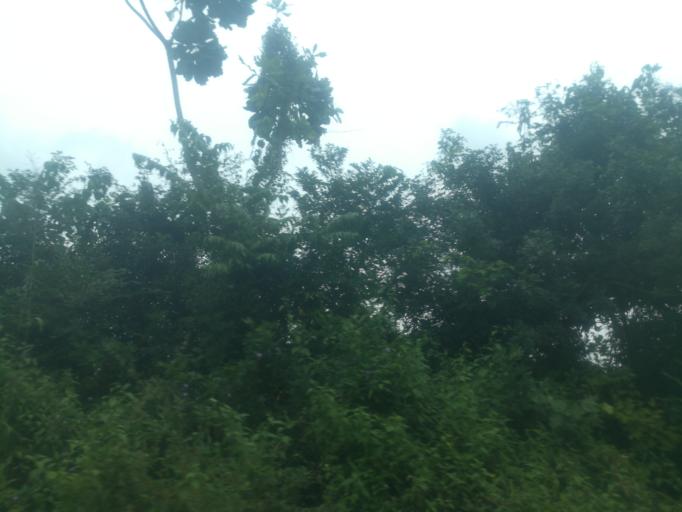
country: NG
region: Ogun
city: Ayetoro
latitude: 7.1027
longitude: 3.1374
